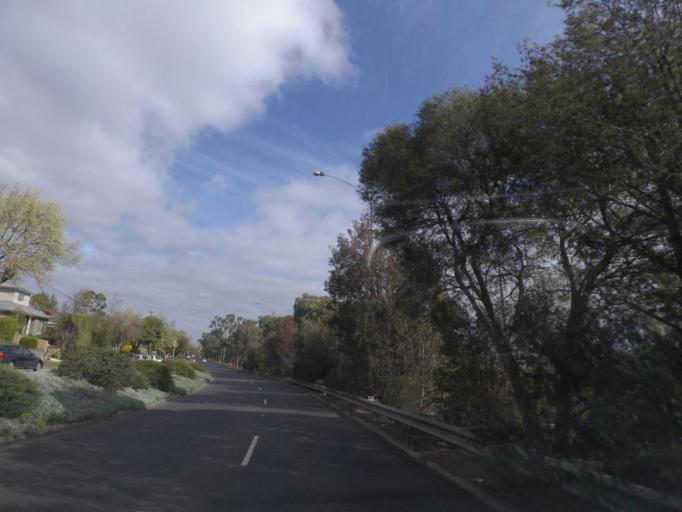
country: AU
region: Victoria
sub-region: Maroondah
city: Croydon South
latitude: -37.8018
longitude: 145.2579
